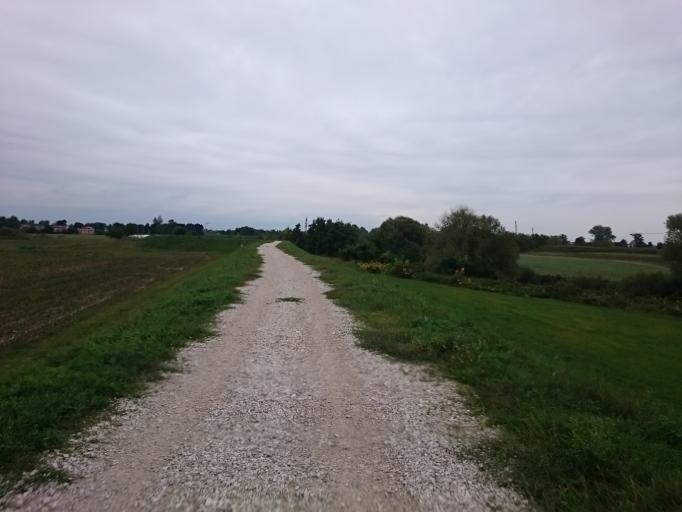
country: IT
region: Veneto
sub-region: Provincia di Vicenza
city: Quinto Vicentino
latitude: 45.5636
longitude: 11.6258
